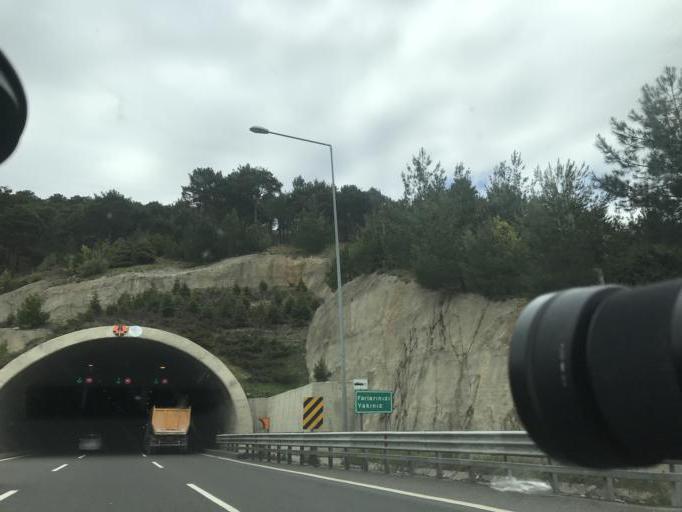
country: TR
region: Nigde
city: Ciftehan
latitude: 37.5083
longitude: 34.8197
